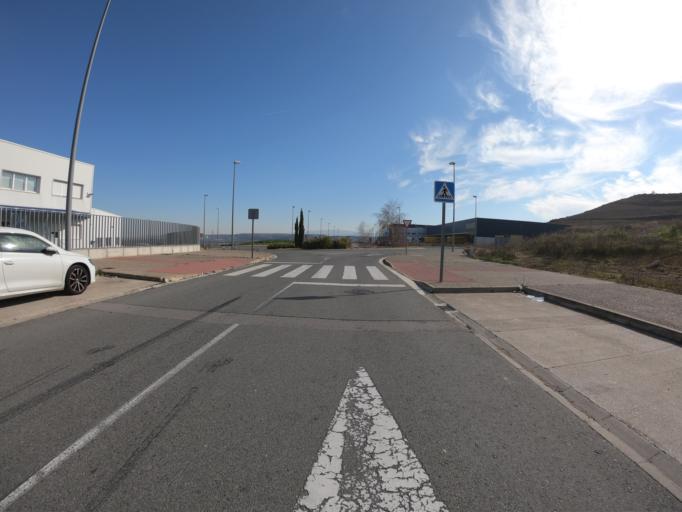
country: ES
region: Basque Country
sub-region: Provincia de Alava
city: Oyon
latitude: 42.4785
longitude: -2.4201
